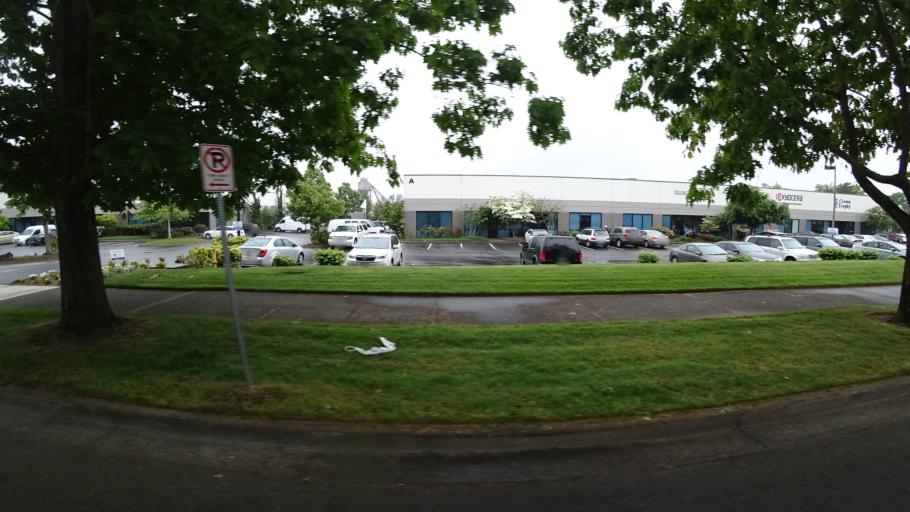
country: US
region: Oregon
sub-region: Washington County
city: Raleigh Hills
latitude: 45.4801
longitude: -122.7787
